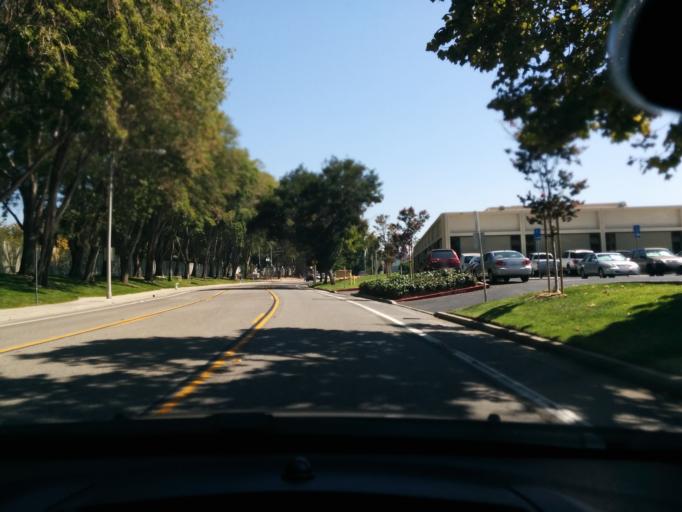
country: US
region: California
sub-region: Santa Clara County
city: Sunnyvale
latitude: 37.3839
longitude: -122.0015
